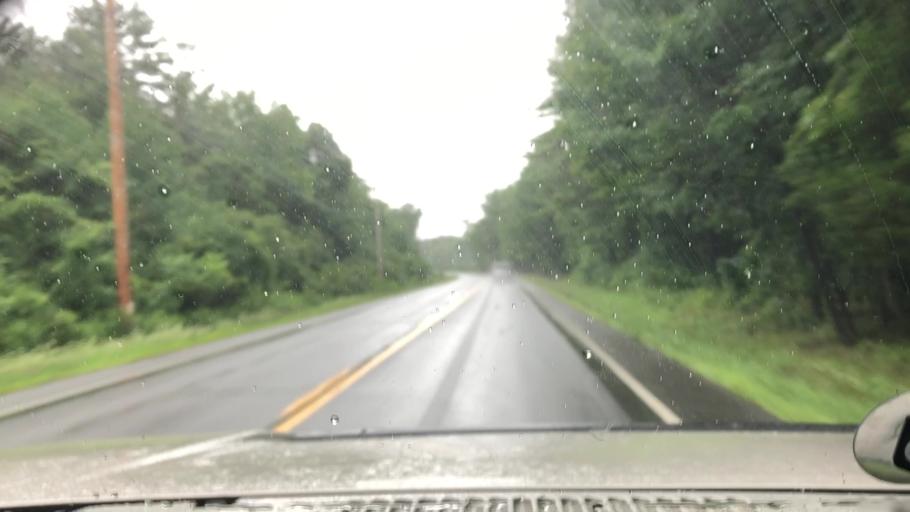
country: US
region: New York
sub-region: Greene County
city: Cairo
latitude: 42.2776
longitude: -73.9793
